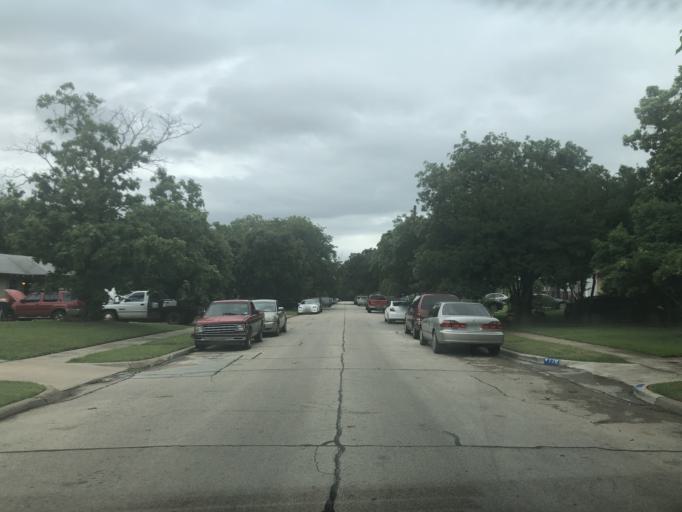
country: US
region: Texas
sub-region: Dallas County
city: Irving
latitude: 32.7985
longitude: -96.9458
